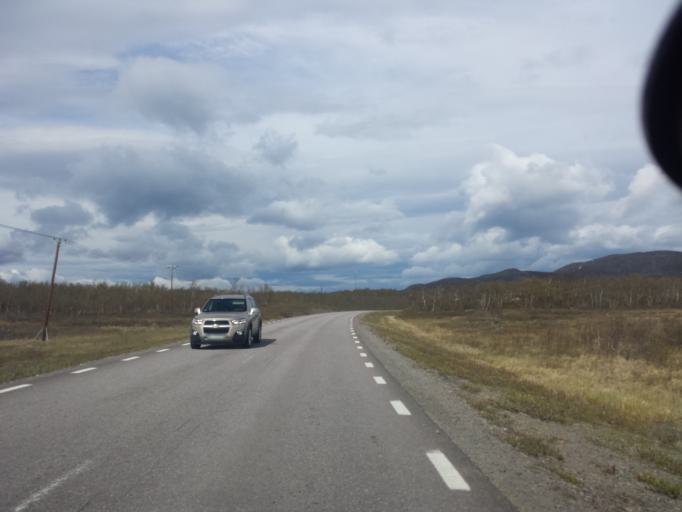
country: SE
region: Norrbotten
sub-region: Kiruna Kommun
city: Kiruna
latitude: 68.1656
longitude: 19.7845
